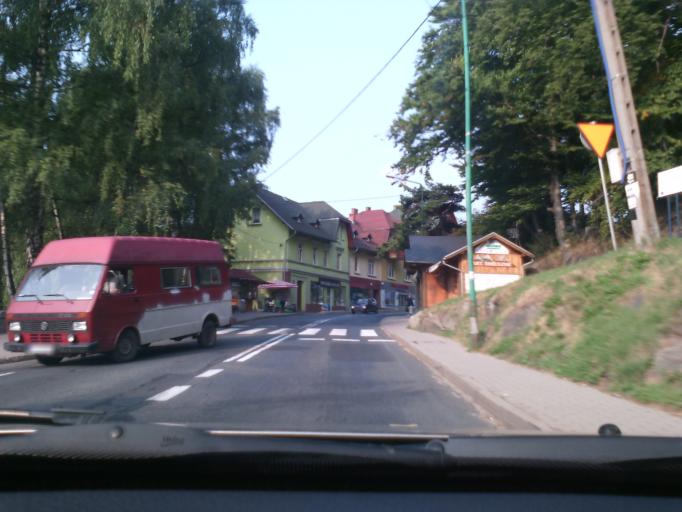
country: PL
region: Lower Silesian Voivodeship
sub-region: Powiat jeleniogorski
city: Szklarska Poreba
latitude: 50.8264
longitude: 15.5224
